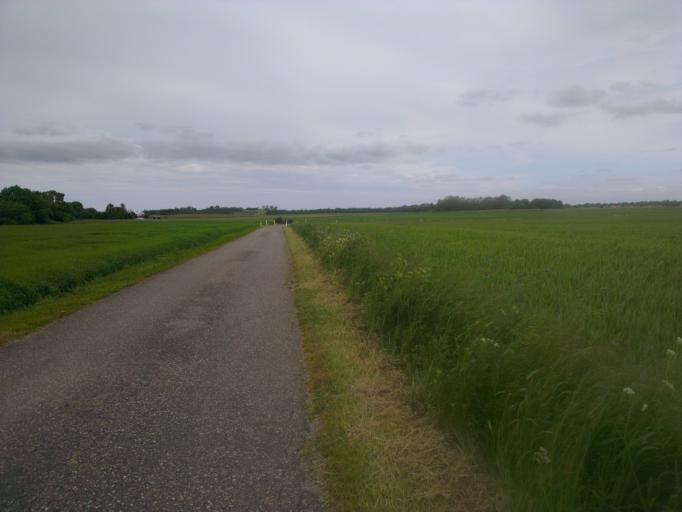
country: DK
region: Capital Region
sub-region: Frederikssund Kommune
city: Frederikssund
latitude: 55.8083
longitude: 12.0769
